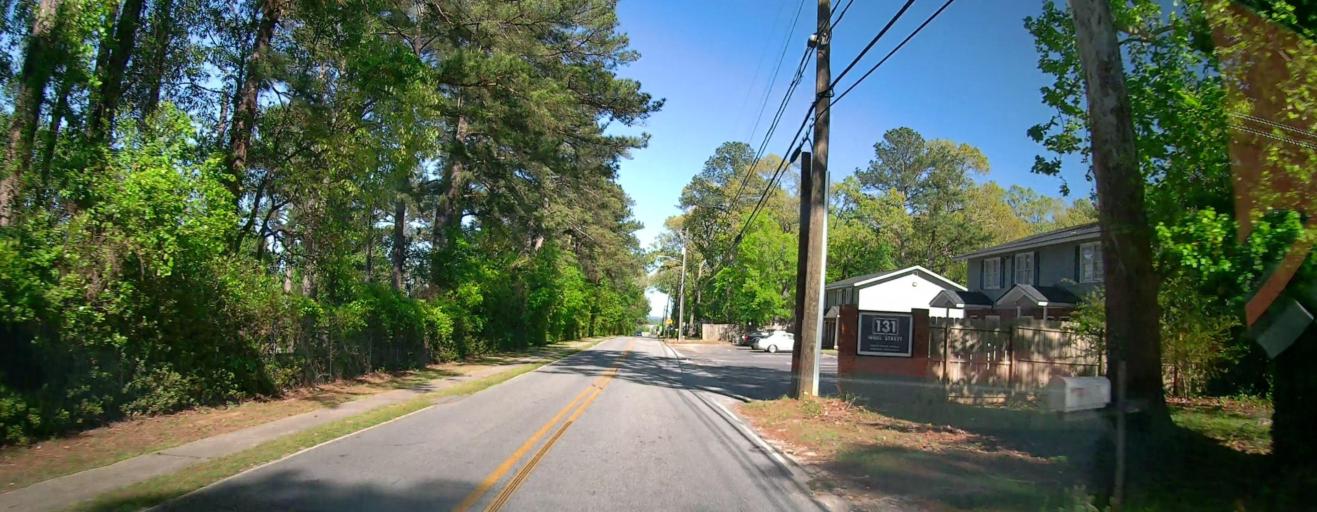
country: US
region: Georgia
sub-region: Houston County
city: Warner Robins
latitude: 32.6017
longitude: -83.6078
